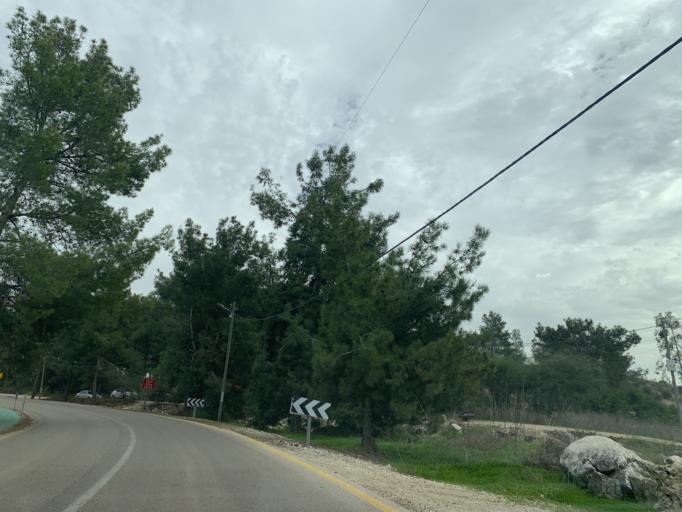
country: IL
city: Nirit
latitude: 32.1434
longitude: 34.9843
